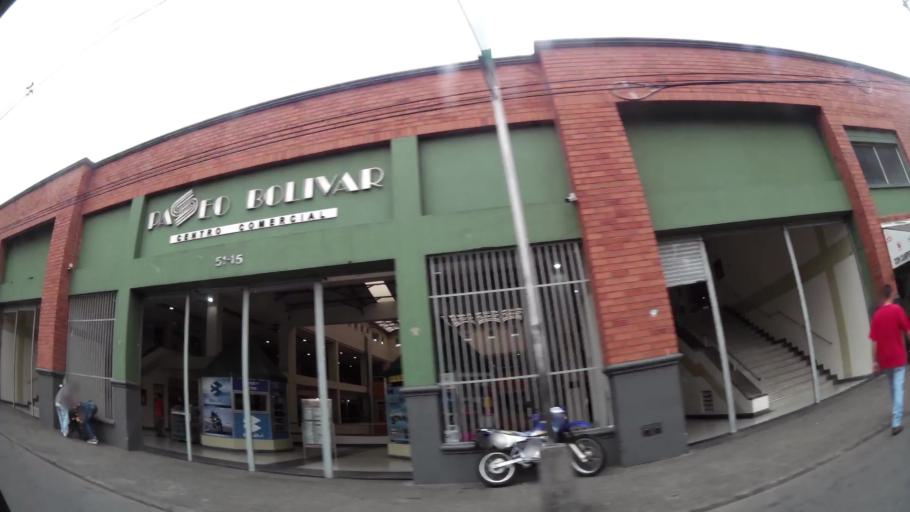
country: CO
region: Antioquia
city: Medellin
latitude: 6.2421
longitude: -75.5722
